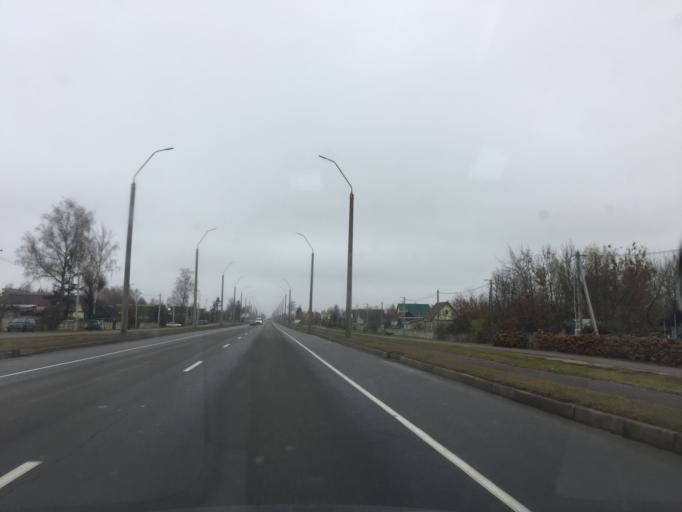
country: BY
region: Mogilev
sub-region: Mahilyowski Rayon
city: Veyno
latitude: 53.8493
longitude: 30.3593
